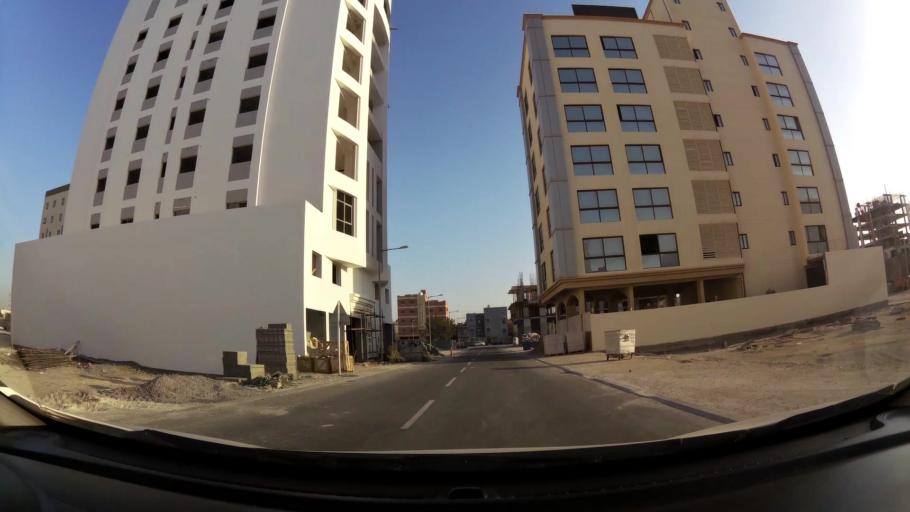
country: BH
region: Manama
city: Jidd Hafs
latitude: 26.2260
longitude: 50.5570
